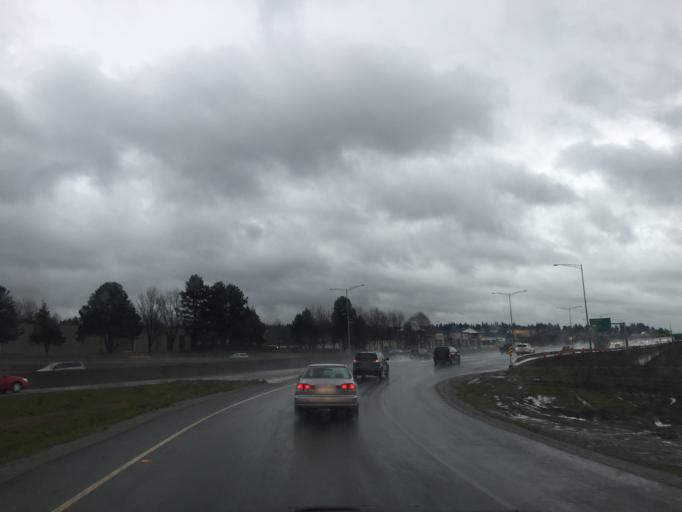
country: CA
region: British Columbia
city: New Westminster
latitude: 49.2336
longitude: -122.8763
